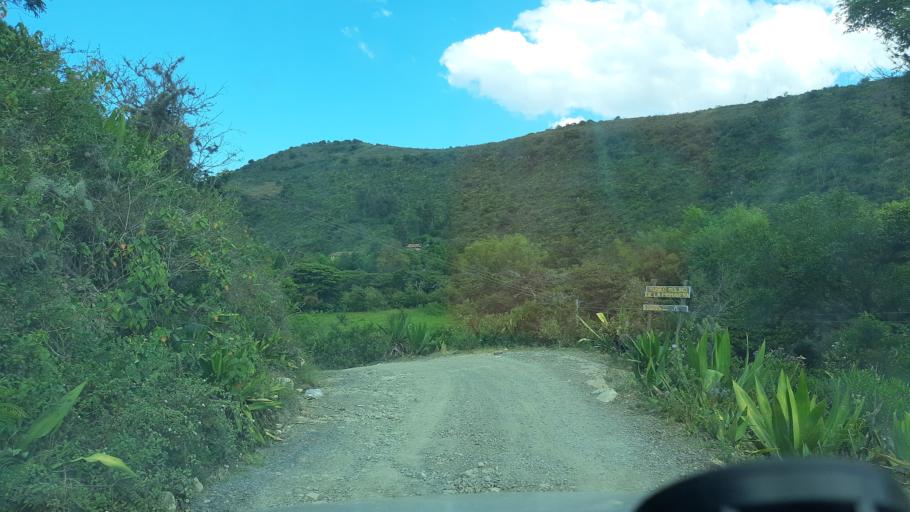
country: CO
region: Boyaca
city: Villa de Leiva
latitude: 5.6795
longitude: -73.5668
